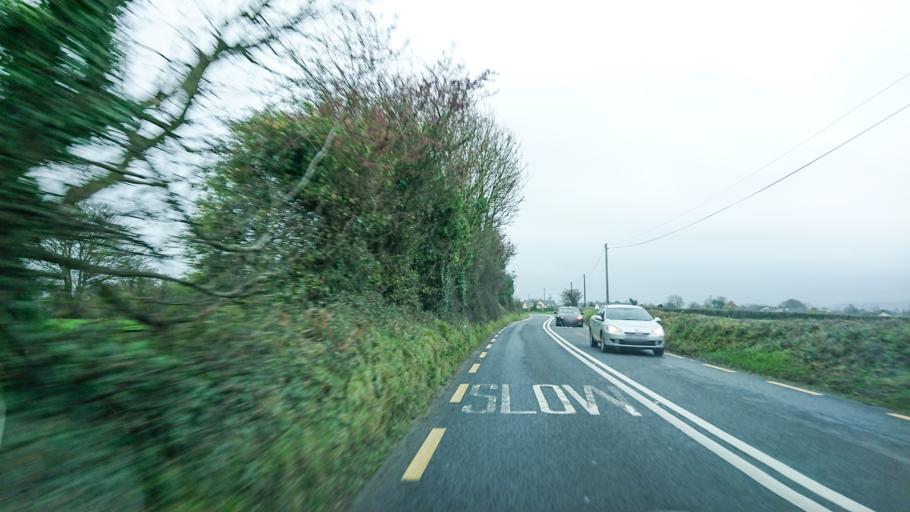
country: IE
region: Leinster
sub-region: Kilkenny
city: Mooncoin
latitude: 52.3028
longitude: -7.2736
